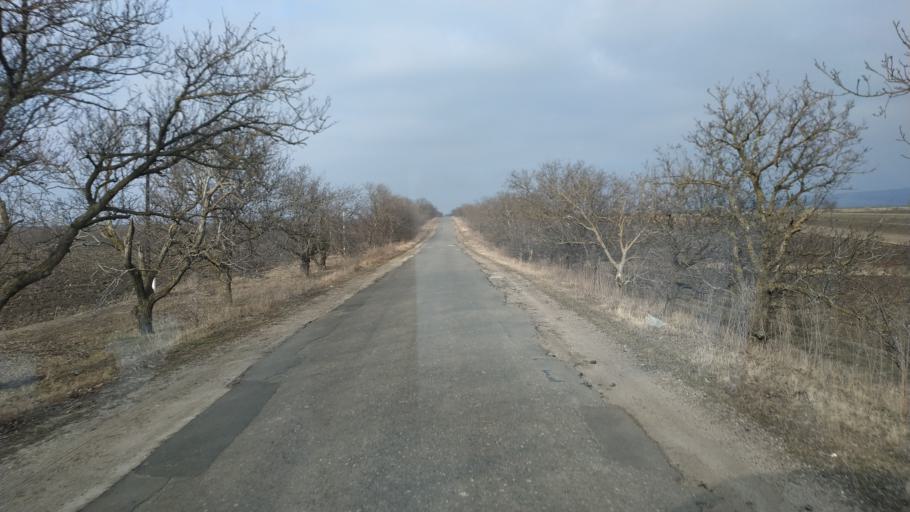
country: MD
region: Hincesti
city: Dancu
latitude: 46.8571
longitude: 28.2887
